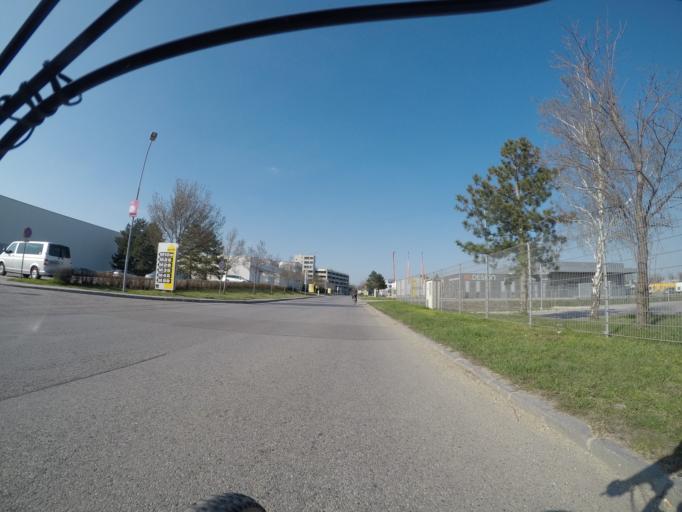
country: AT
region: Lower Austria
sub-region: Politischer Bezirk Modling
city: Neu-Guntramsdorf
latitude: 48.0718
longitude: 16.3156
